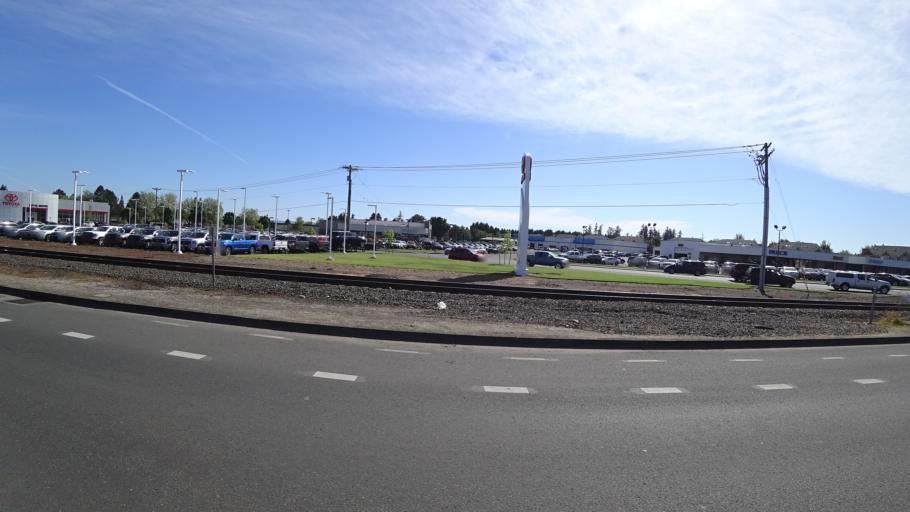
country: US
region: Oregon
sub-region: Washington County
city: Hillsboro
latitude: 45.5097
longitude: -122.9682
